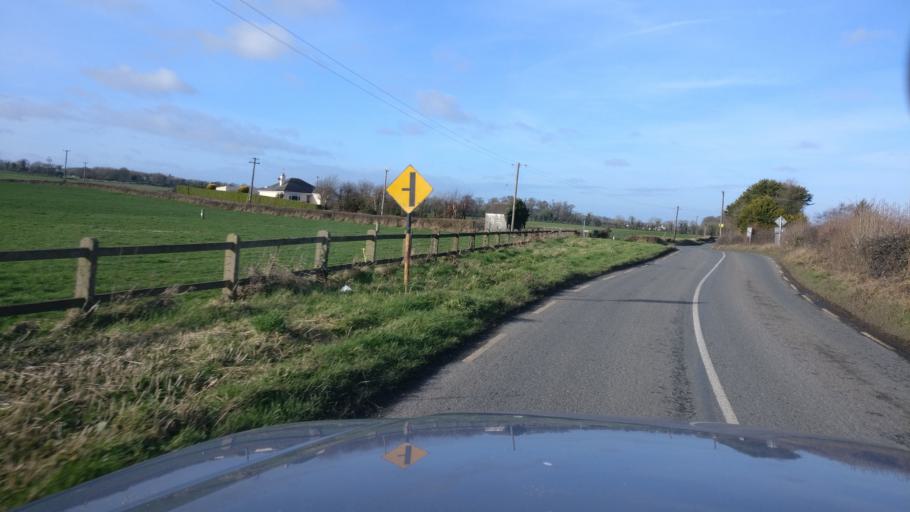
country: IE
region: Leinster
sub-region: Laois
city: Stradbally
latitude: 52.9702
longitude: -7.2115
